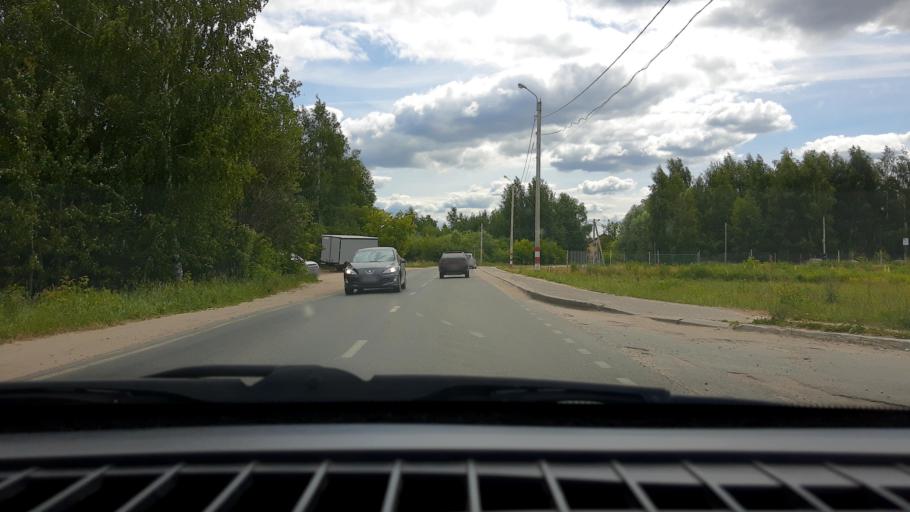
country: RU
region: Nizjnij Novgorod
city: Bor
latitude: 56.3868
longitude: 44.0422
